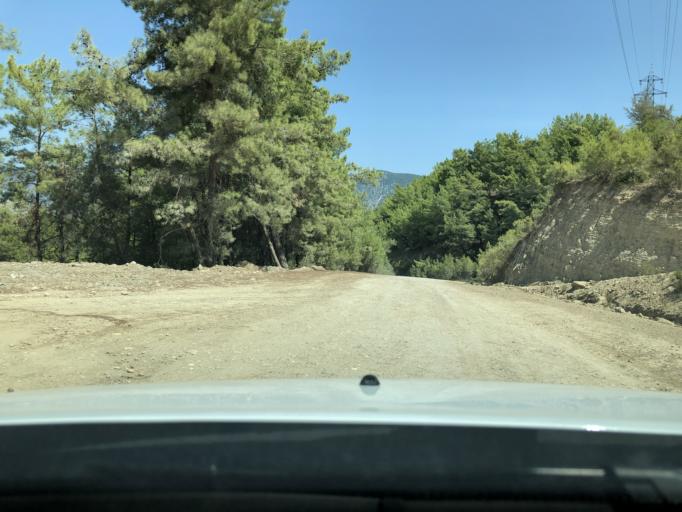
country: TR
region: Antalya
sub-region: Manavgat
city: Manavgat
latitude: 36.8367
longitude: 31.5355
